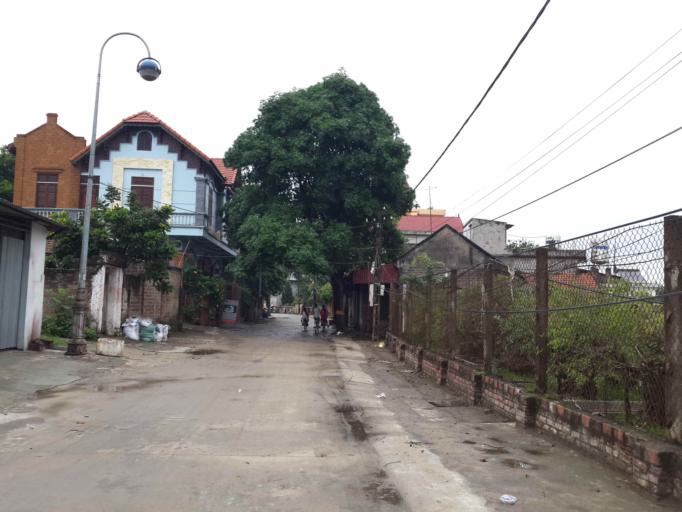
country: VN
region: Ha Noi
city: Son Tay
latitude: 21.1600
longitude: 105.4694
